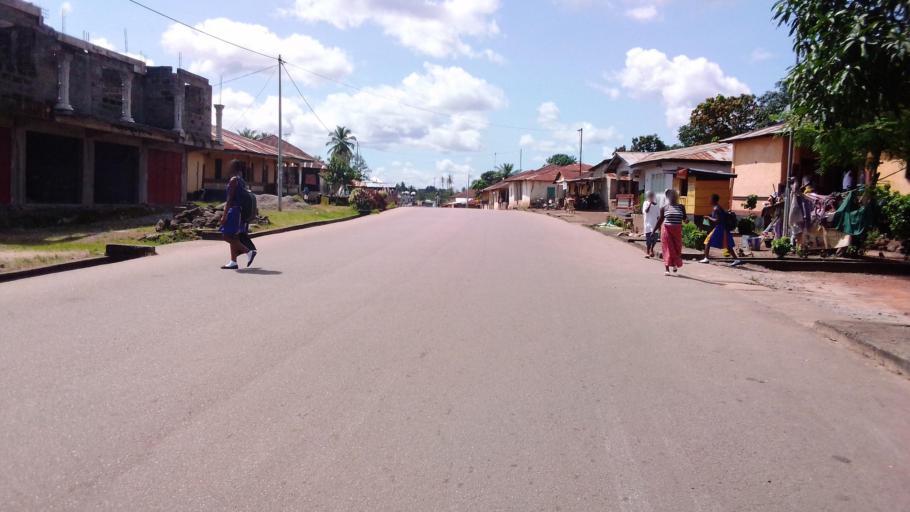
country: SL
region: Northern Province
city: Makeni
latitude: 8.8858
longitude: -12.0471
